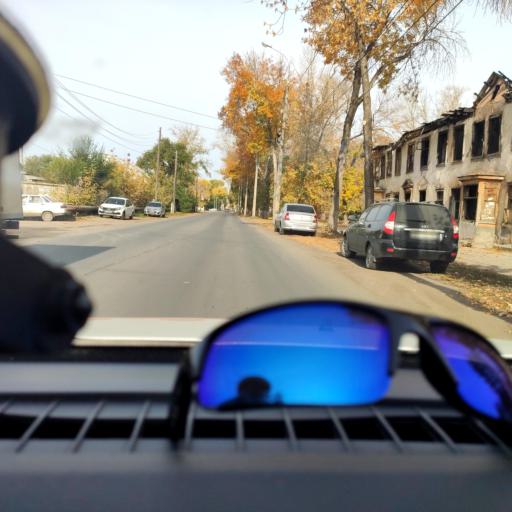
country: RU
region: Samara
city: Samara
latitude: 53.1104
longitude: 50.0766
